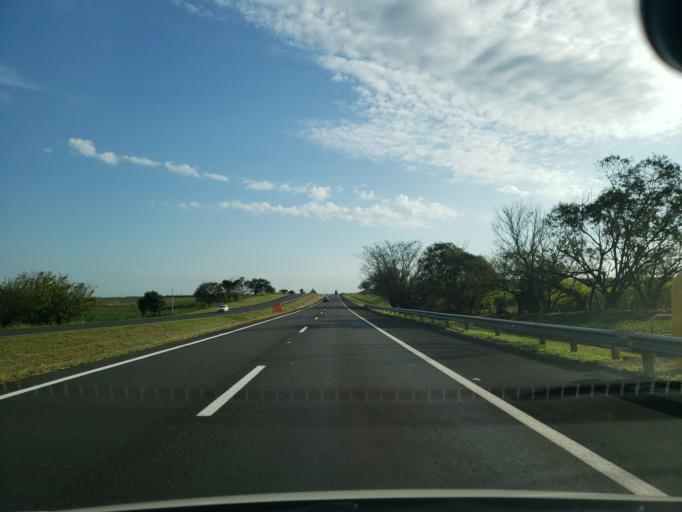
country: BR
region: Sao Paulo
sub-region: Valparaiso
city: Valparaiso
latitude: -21.2065
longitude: -50.8142
